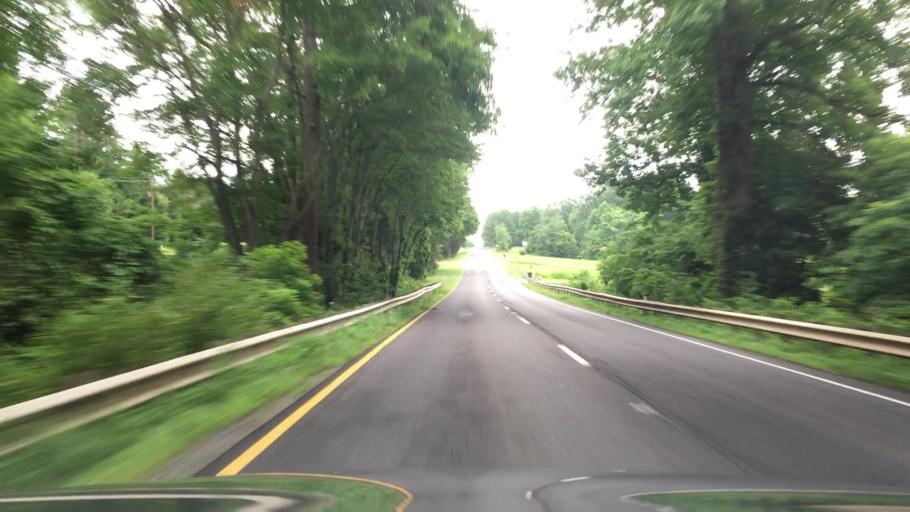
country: US
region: Virginia
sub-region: Spotsylvania County
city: Spotsylvania
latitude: 38.3219
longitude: -77.7043
